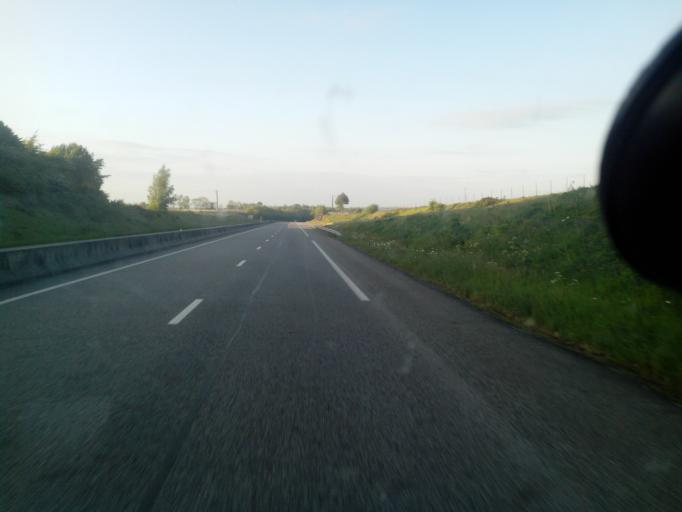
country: FR
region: Haute-Normandie
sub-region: Departement de la Seine-Maritime
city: Foucarmont
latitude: 49.8318
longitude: 1.5265
